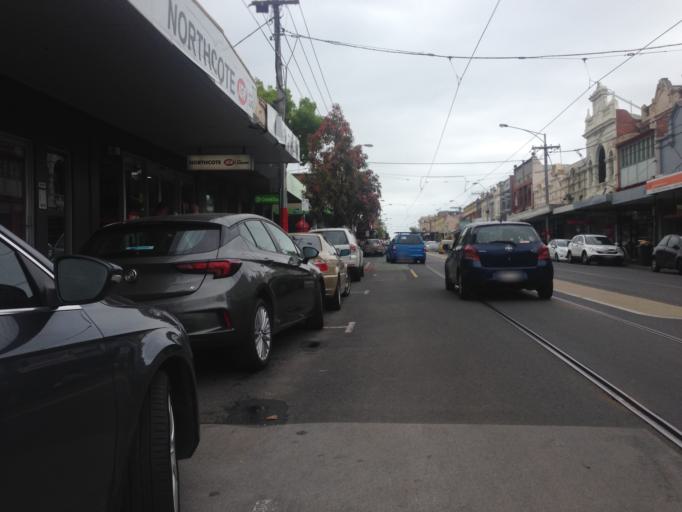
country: AU
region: Victoria
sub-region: Darebin
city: Northcote
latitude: -37.7717
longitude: 144.9986
